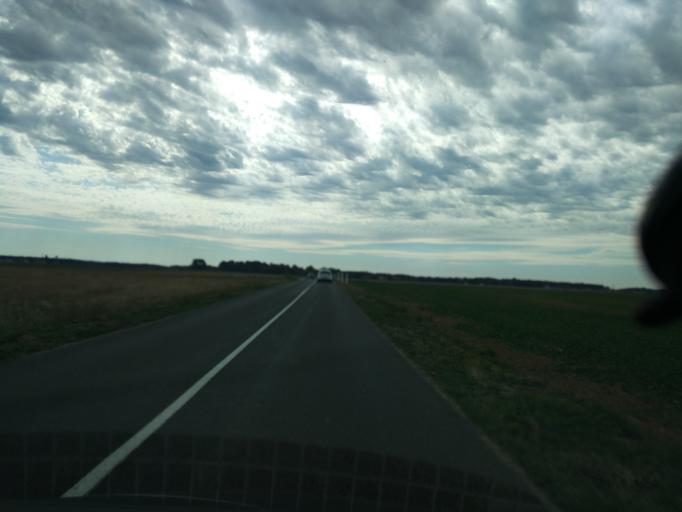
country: FR
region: Ile-de-France
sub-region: Departement de l'Essonne
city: Gometz-la-Ville
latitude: 48.6596
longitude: 2.1252
